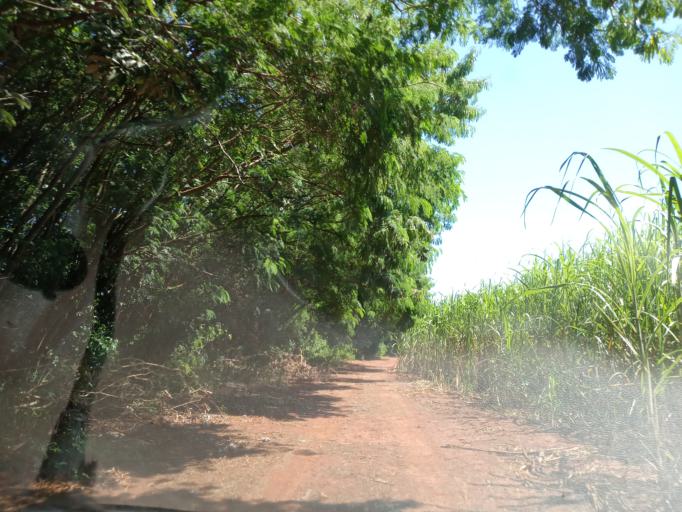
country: BR
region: Goias
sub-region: Itumbiara
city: Itumbiara
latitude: -18.4436
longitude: -49.1416
